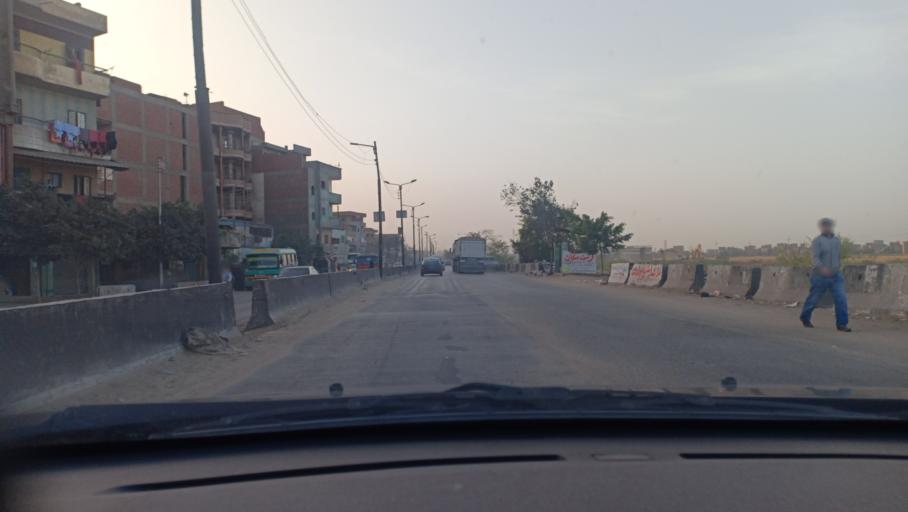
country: EG
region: Muhafazat al Gharbiyah
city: Zifta
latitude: 30.6827
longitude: 31.2814
